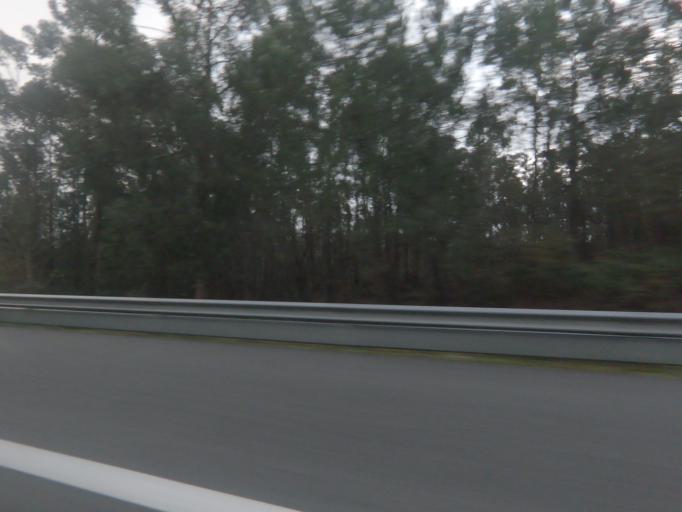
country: PT
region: Viana do Castelo
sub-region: Ponte de Lima
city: Ponte de Lima
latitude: 41.7513
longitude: -8.5563
